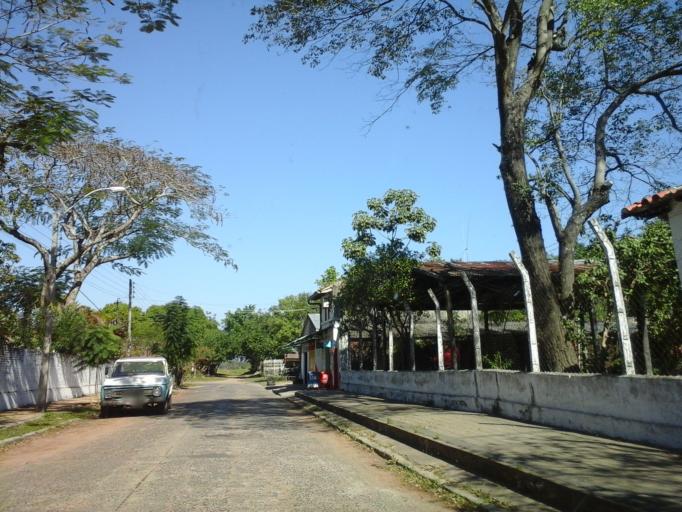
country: PY
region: Neembucu
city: Pilar
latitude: -26.8558
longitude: -58.3106
